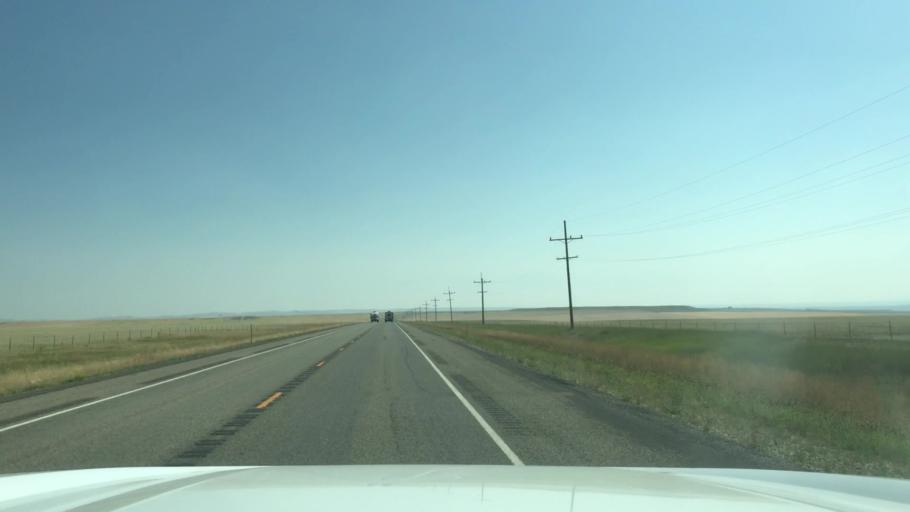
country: US
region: Montana
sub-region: Wheatland County
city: Harlowton
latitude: 46.5027
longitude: -109.7662
